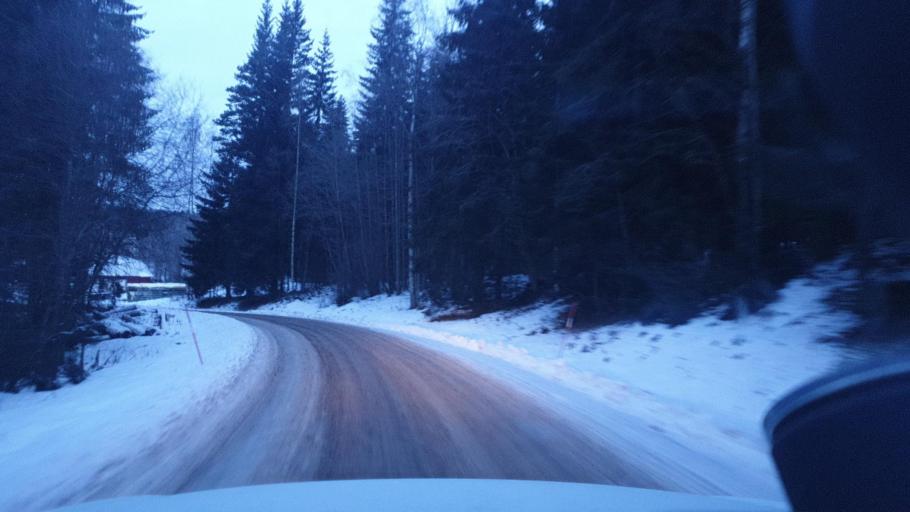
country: SE
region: Vaermland
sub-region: Eda Kommun
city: Amotfors
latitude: 59.8239
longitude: 12.4498
